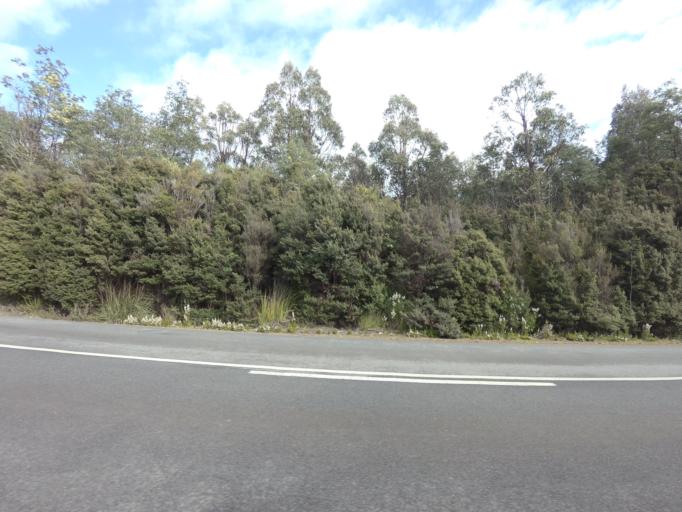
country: AU
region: Tasmania
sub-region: Huon Valley
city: Geeveston
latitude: -43.3675
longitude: 146.9587
